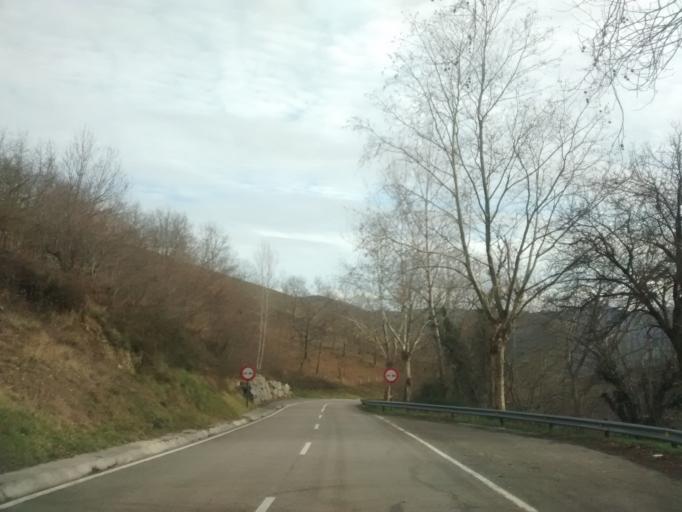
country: ES
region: Cantabria
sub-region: Provincia de Cantabria
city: Ruente
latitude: 43.2343
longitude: -4.3185
